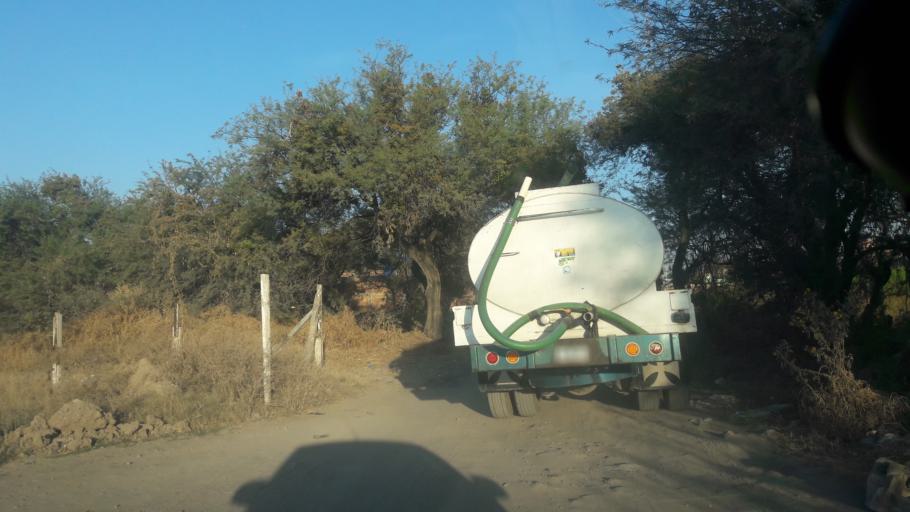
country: MX
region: Guanajuato
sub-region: Leon
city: Medina
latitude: 21.1680
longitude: -101.6374
